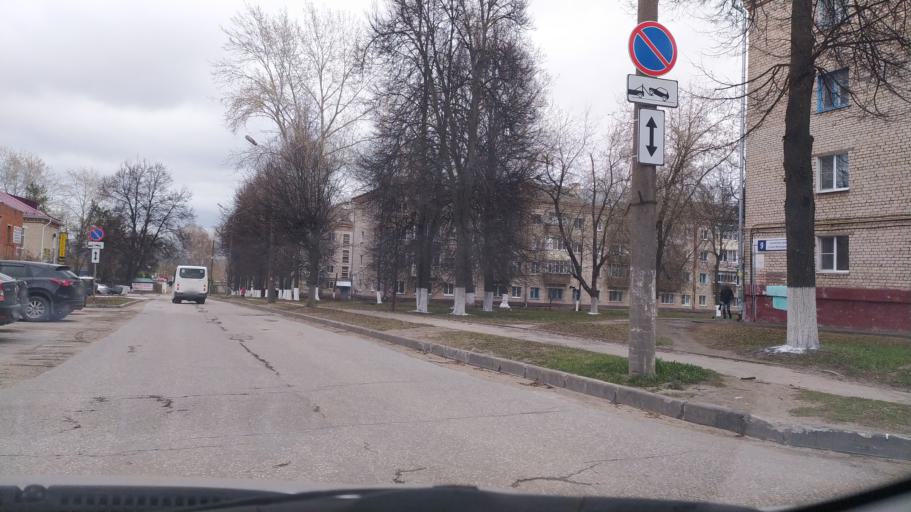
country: RU
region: Chuvashia
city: Novocheboksarsk
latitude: 56.1183
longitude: 47.4998
